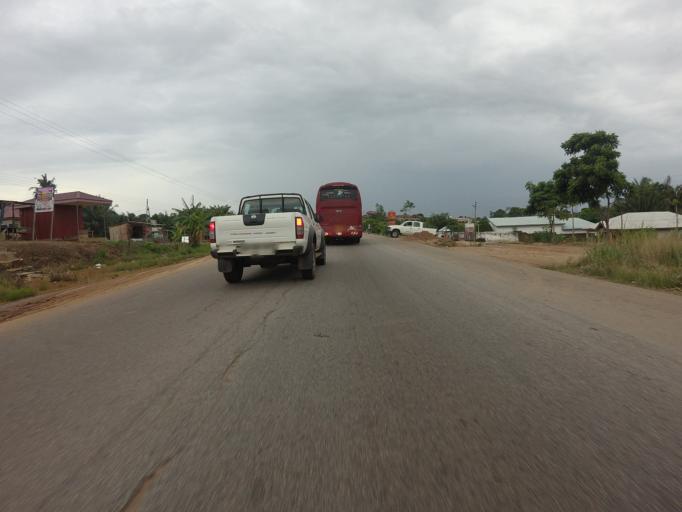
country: GH
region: Ashanti
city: Konongo
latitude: 6.6170
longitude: -1.1778
